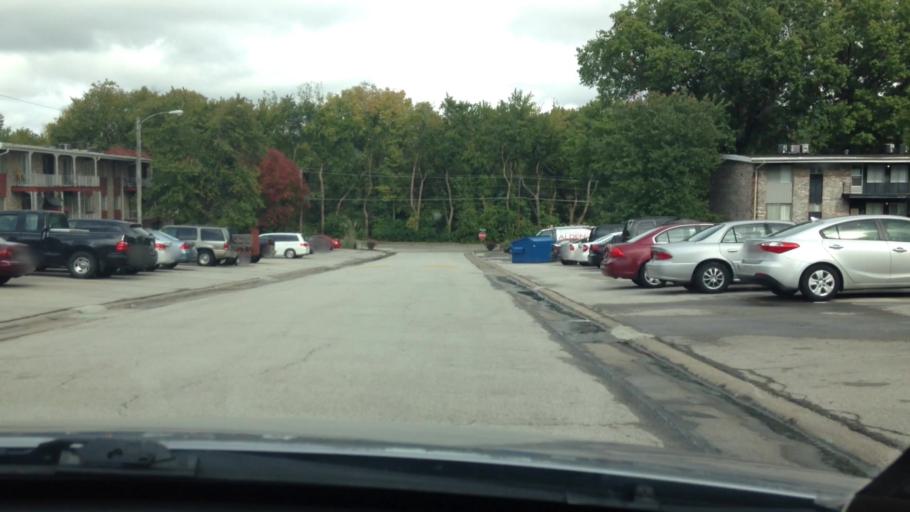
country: US
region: Kansas
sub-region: Leavenworth County
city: Leavenworth
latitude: 39.3020
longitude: -94.9364
